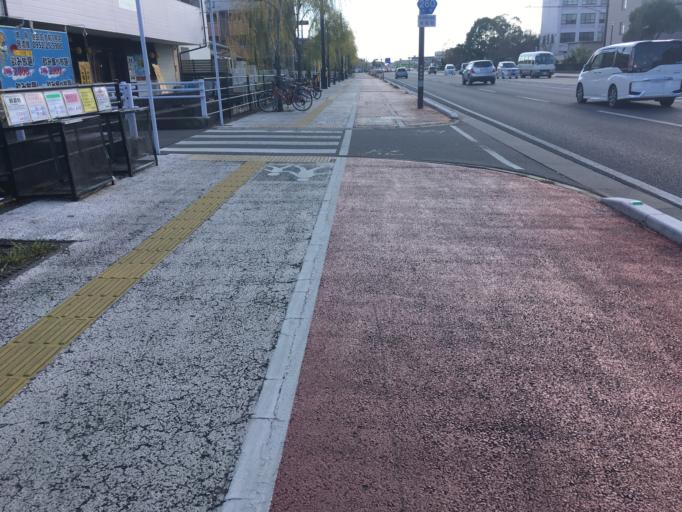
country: JP
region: Saga Prefecture
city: Saga-shi
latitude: 33.2439
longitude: 130.2937
